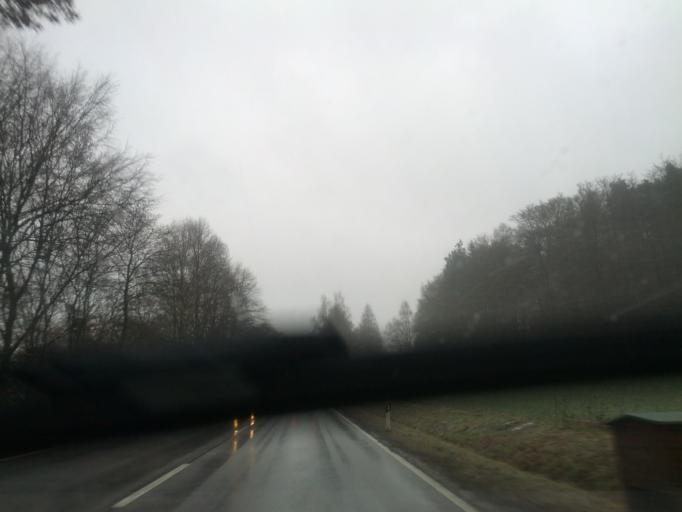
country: DE
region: Thuringia
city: Gerstungen
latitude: 51.0249
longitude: 10.0268
